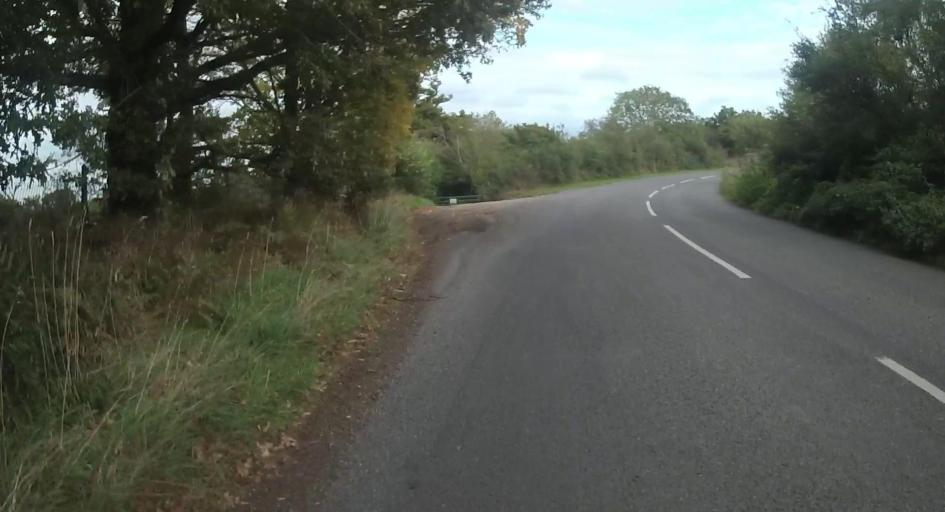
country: GB
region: England
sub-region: Hampshire
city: Odiham
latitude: 51.2918
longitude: -0.8949
